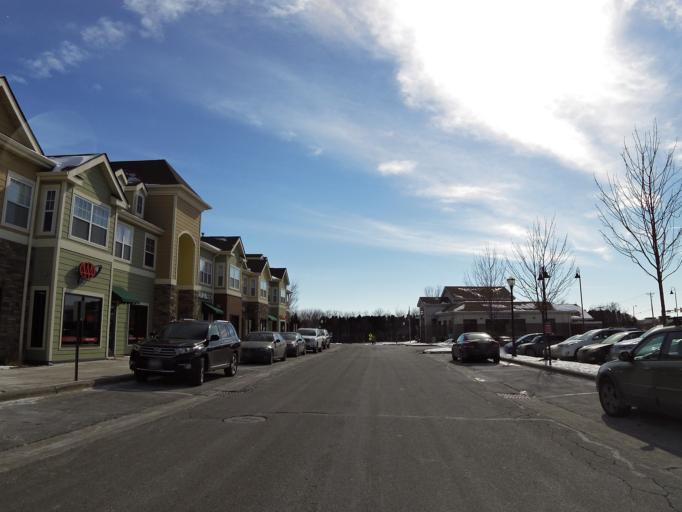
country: US
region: Minnesota
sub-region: Washington County
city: Lake Elmo
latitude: 44.9429
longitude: -92.9023
